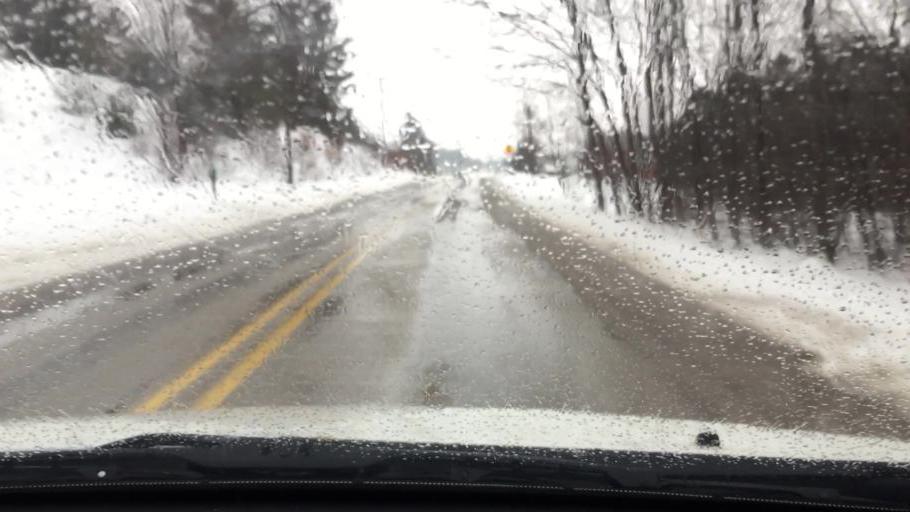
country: US
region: Michigan
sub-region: Charlevoix County
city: East Jordan
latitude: 45.1098
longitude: -85.1292
